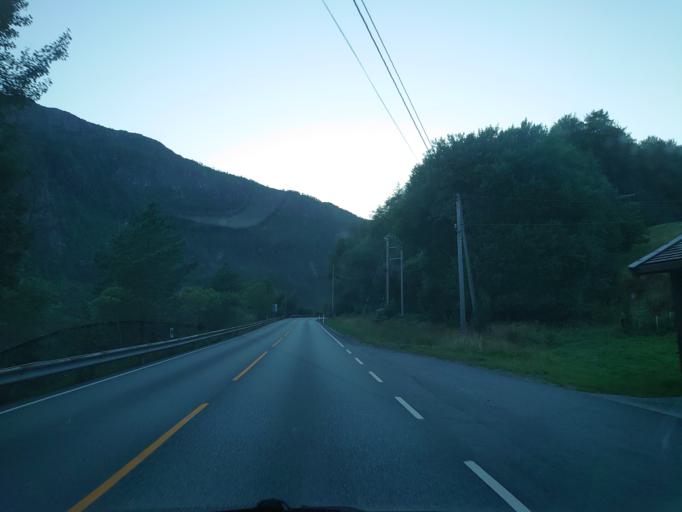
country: NO
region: Hordaland
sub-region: Osteroy
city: Lonevag
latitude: 60.6982
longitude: 5.5712
